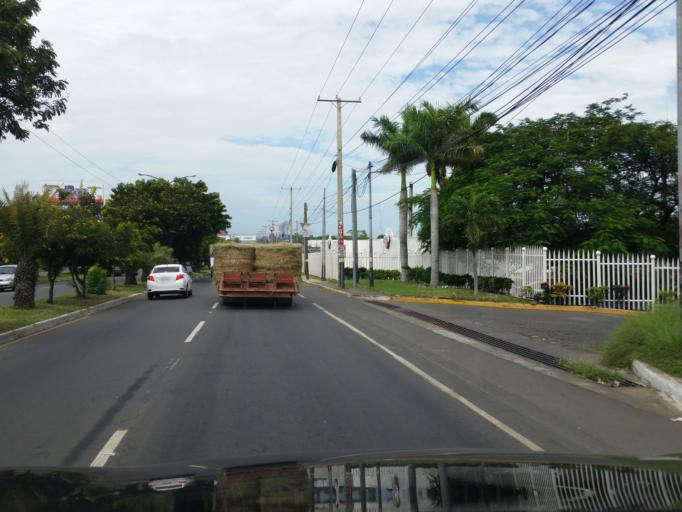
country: NI
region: Managua
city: Managua
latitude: 12.1511
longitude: -86.2285
